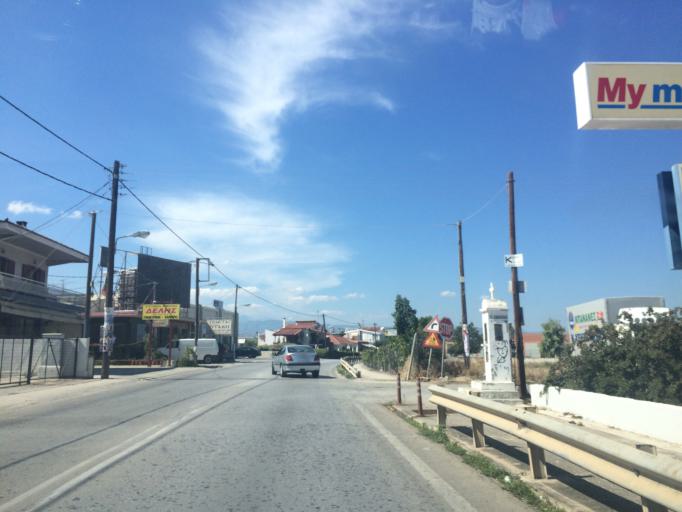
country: GR
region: Peloponnese
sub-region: Nomos Korinthias
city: Lekhaio
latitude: 37.9326
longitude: 22.8512
